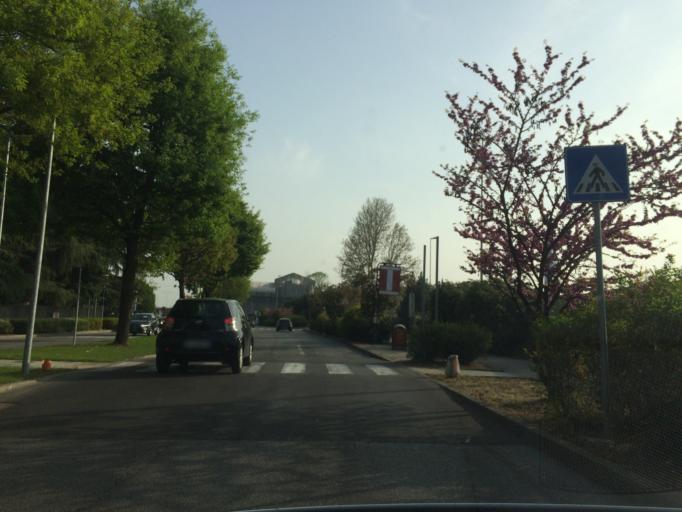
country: IT
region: Lombardy
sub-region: Provincia di Brescia
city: Brescia
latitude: 45.5169
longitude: 10.2152
